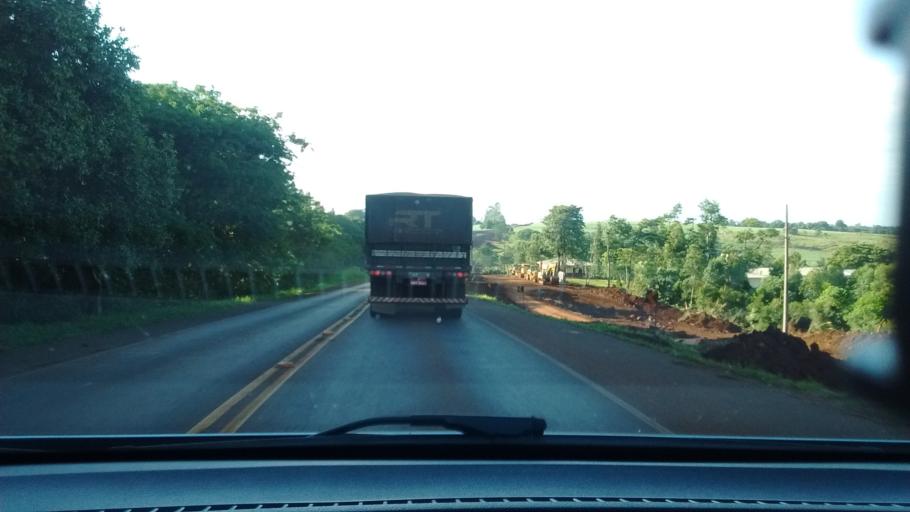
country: BR
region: Parana
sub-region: Cascavel
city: Cascavel
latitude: -25.2105
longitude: -53.5971
